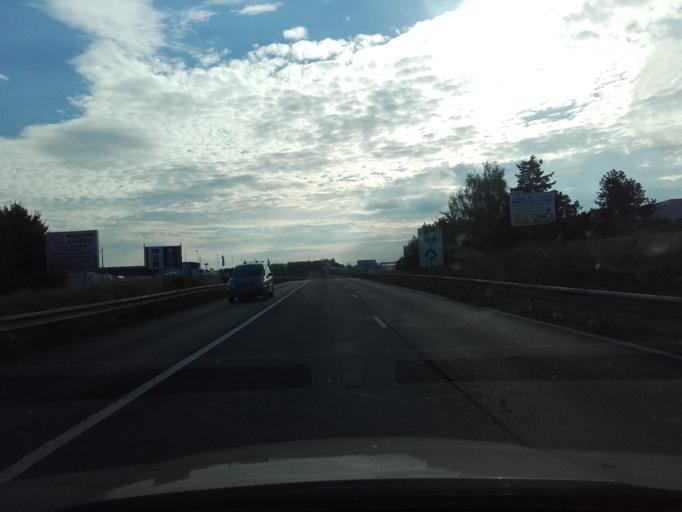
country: FR
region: Centre
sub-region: Departement d'Indre-et-Loire
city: Parcay-Meslay
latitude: 47.4508
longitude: 0.7295
